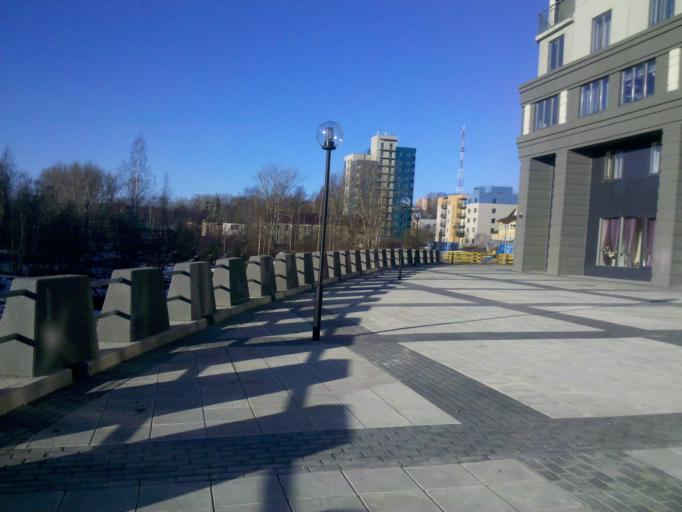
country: RU
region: Republic of Karelia
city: Petrozavodsk
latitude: 61.7773
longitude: 34.3529
